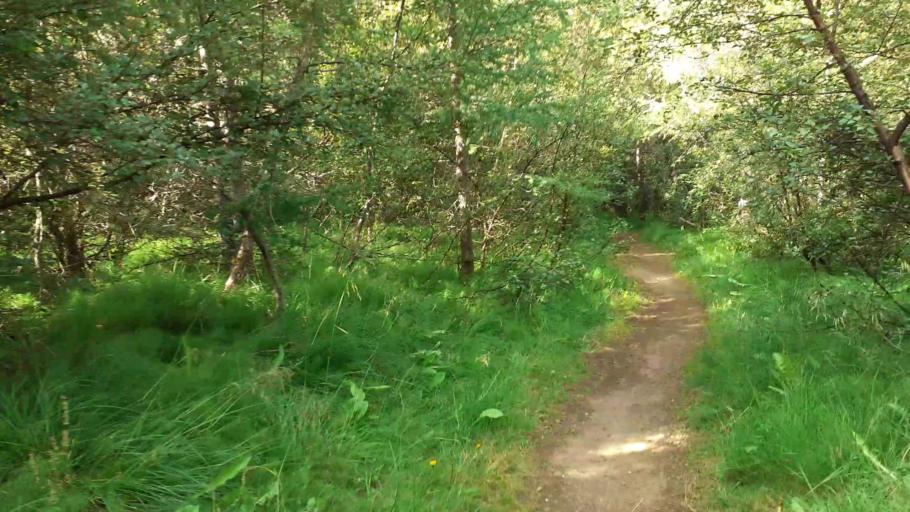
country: IS
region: Northeast
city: Akureyri
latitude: 65.6399
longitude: -18.0947
